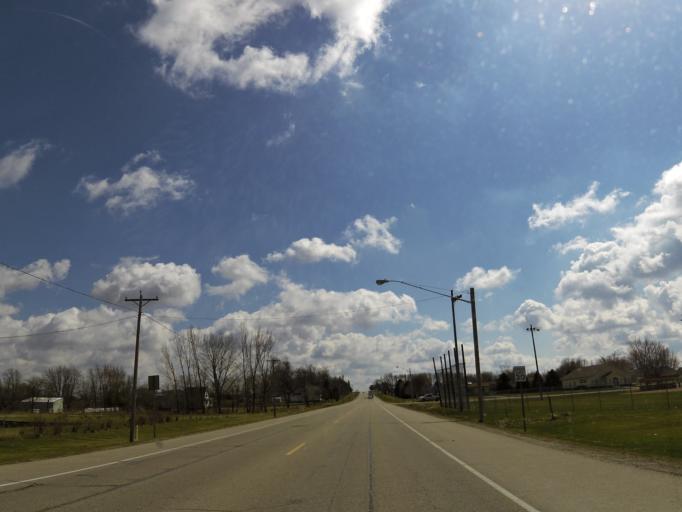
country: US
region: Minnesota
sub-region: Dodge County
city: Dodge Center
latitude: 44.1475
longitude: -92.8994
